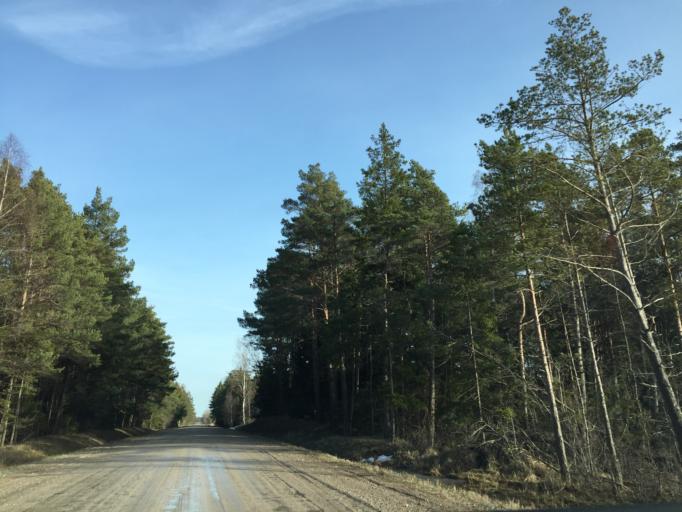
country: EE
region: Saare
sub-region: Kuressaare linn
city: Kuressaare
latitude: 58.3136
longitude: 21.9843
